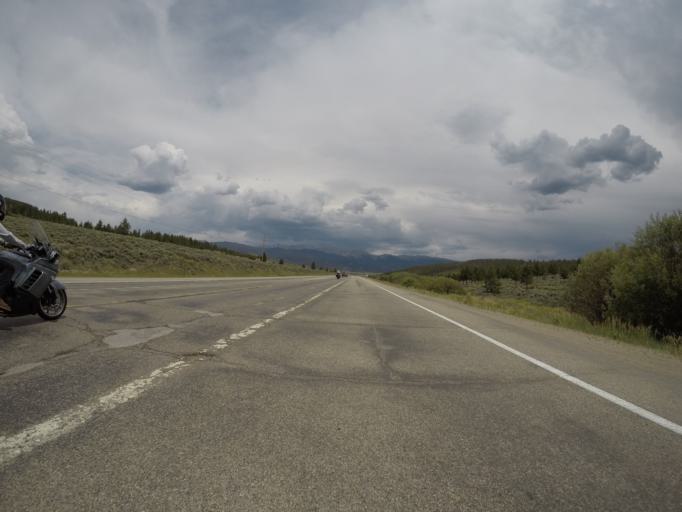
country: US
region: Colorado
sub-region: Grand County
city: Fraser
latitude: 39.9952
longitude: -105.8719
